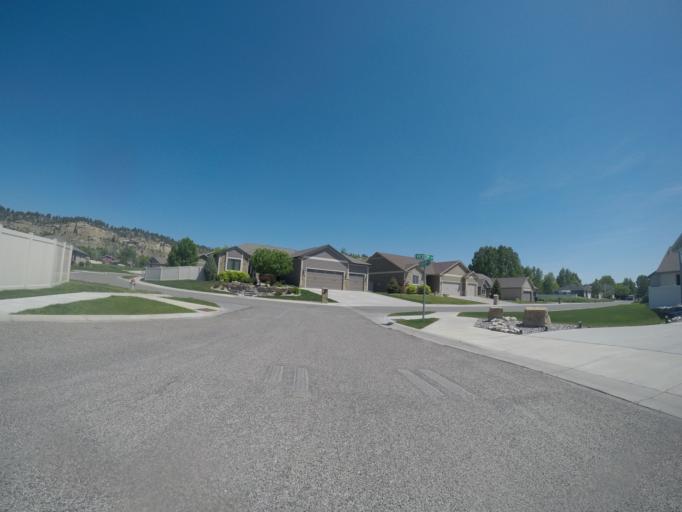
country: US
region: Montana
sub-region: Yellowstone County
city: Billings
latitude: 45.7966
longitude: -108.6100
